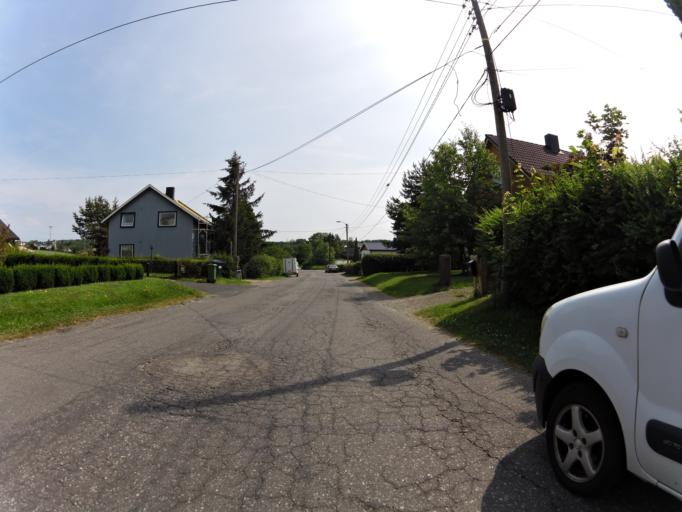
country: NO
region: Ostfold
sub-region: Fredrikstad
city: Fredrikstad
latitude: 59.2435
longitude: 10.9936
